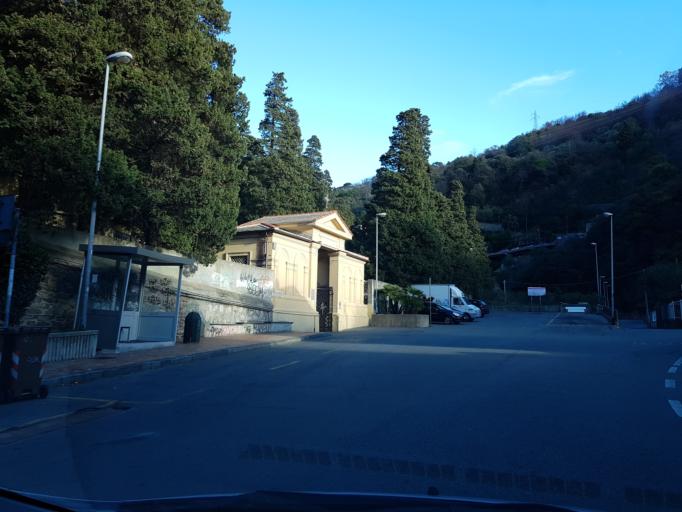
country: IT
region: Liguria
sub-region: Provincia di Genova
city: Bogliasco
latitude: 44.3898
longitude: 9.0366
